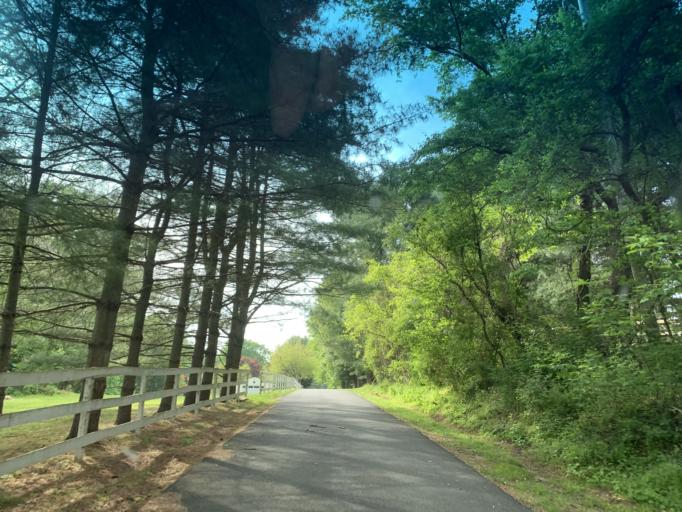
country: US
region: Maryland
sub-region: Baltimore County
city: Perry Hall
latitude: 39.4498
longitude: -76.4616
